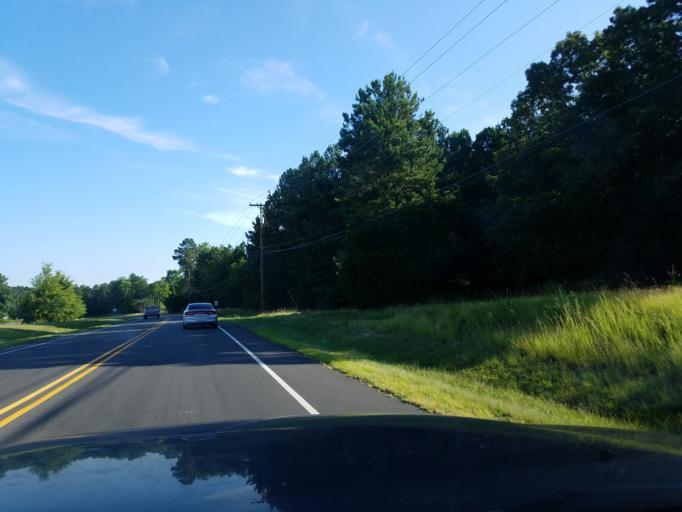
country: US
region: North Carolina
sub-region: Granville County
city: Butner
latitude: 36.1244
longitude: -78.7506
